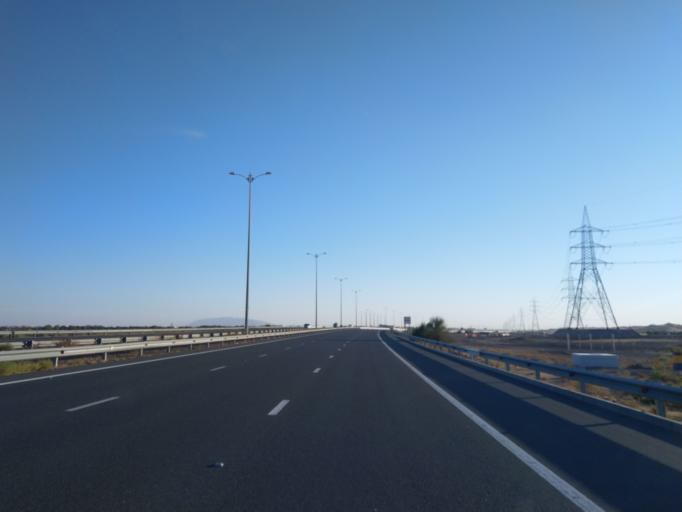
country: OM
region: Al Buraimi
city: Al Buraymi
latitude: 24.3760
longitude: 55.7974
